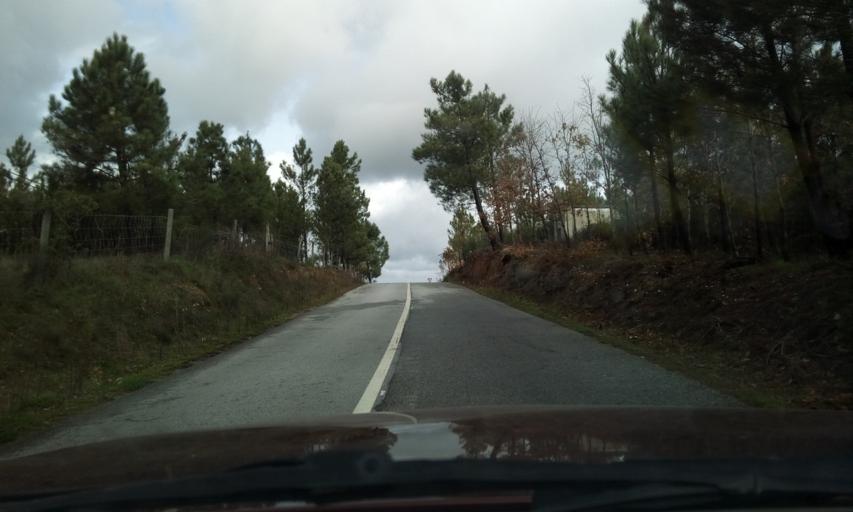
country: PT
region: Guarda
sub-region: Fornos de Algodres
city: Fornos de Algodres
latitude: 40.6377
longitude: -7.5476
